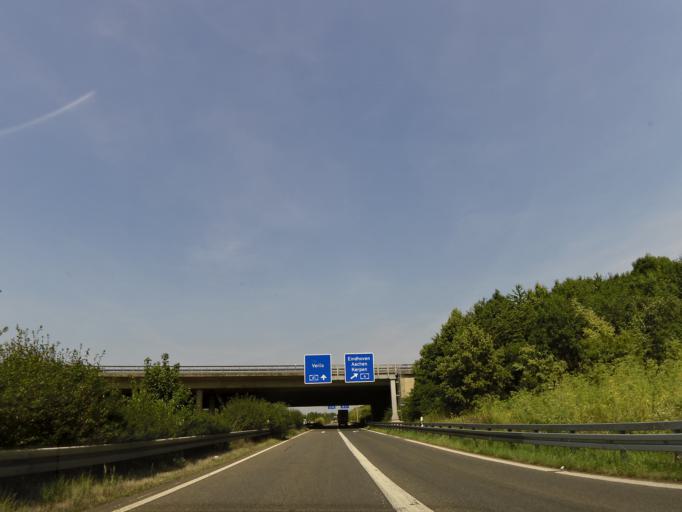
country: DE
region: North Rhine-Westphalia
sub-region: Regierungsbezirk Koln
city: Kerpen
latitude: 50.8937
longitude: 6.6964
